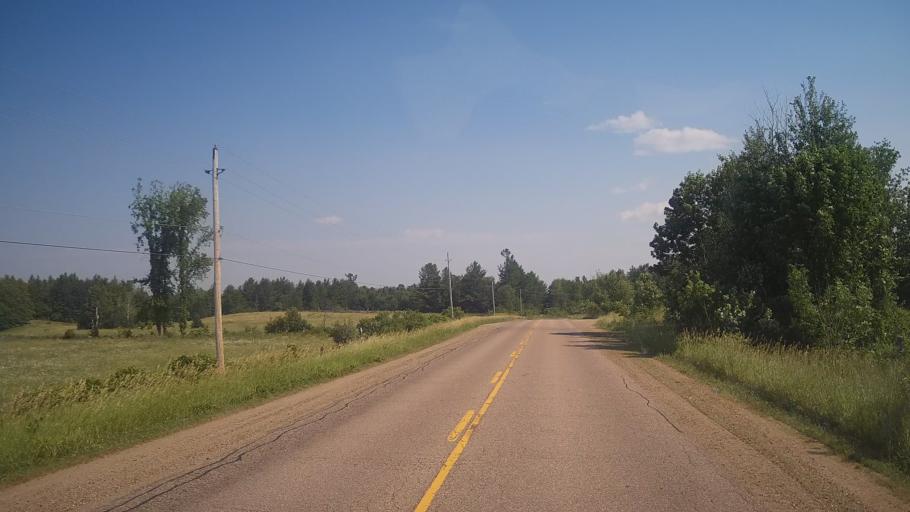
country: CA
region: Ontario
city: Pembroke
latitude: 45.5902
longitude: -77.2275
